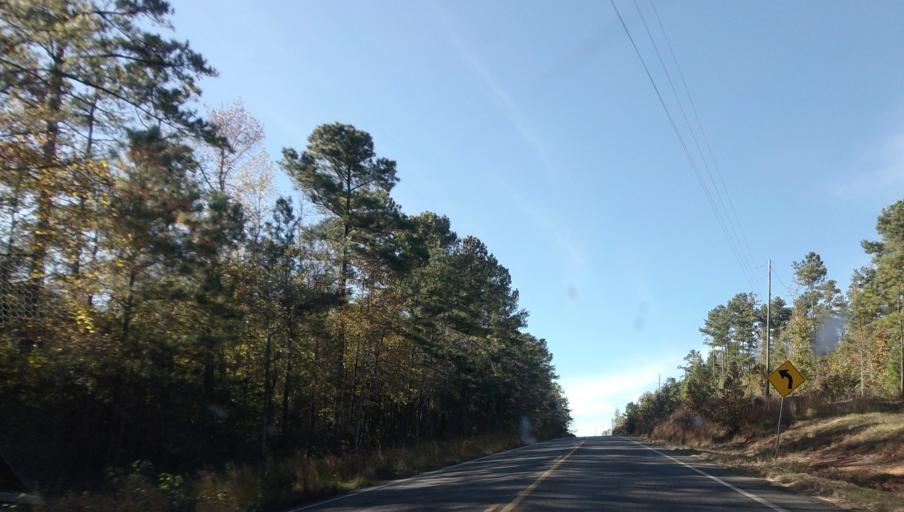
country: US
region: Georgia
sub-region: Talbot County
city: Talbotton
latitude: 32.6789
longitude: -84.6405
